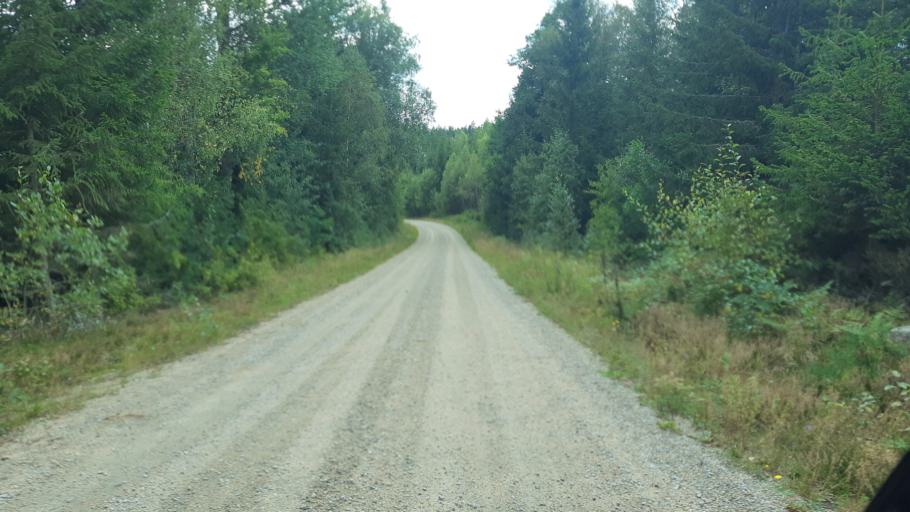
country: SE
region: Blekinge
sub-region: Ronneby Kommun
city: Brakne-Hoby
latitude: 56.4298
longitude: 15.1847
